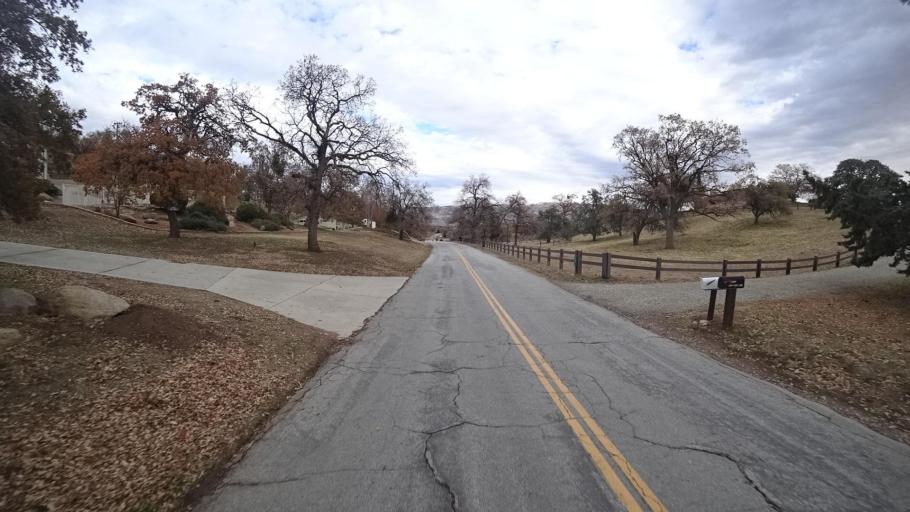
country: US
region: California
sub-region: Kern County
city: Golden Hills
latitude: 35.1161
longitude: -118.5144
